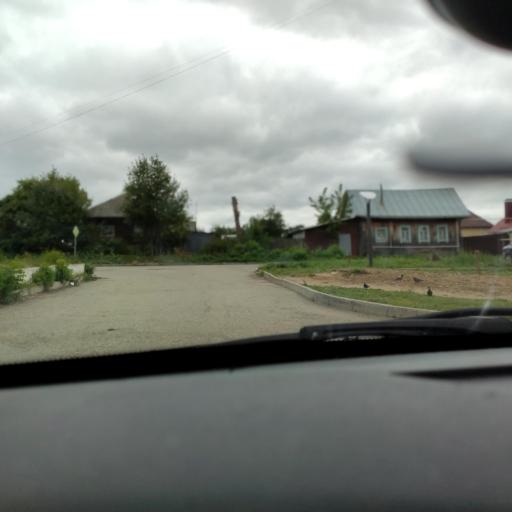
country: RU
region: Perm
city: Dobryanka
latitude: 58.4613
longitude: 56.3976
